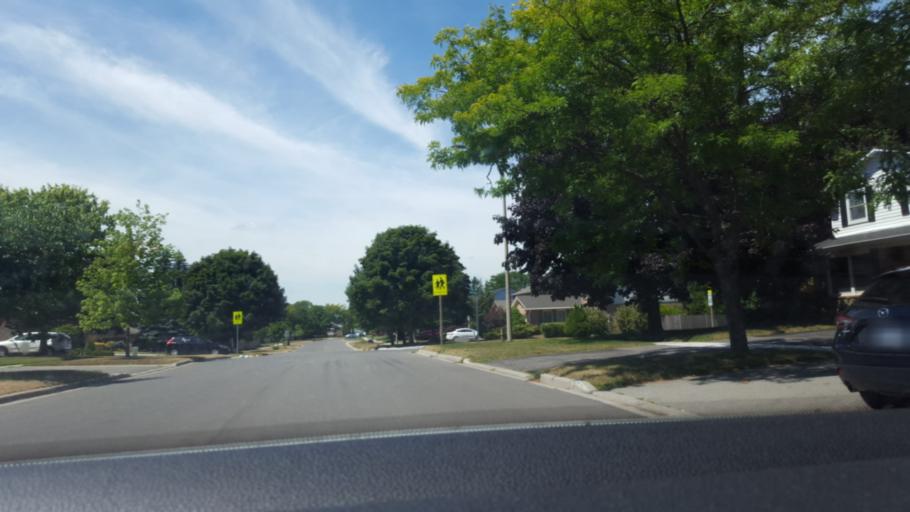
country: CA
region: Ontario
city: Ancaster
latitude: 43.2071
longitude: -79.9875
